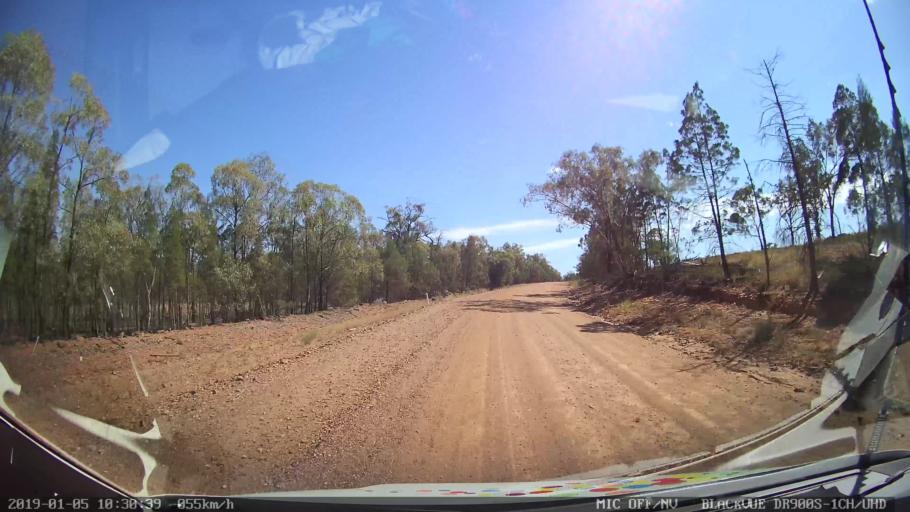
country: AU
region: New South Wales
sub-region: Gilgandra
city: Gilgandra
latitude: -31.5305
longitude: 148.9249
